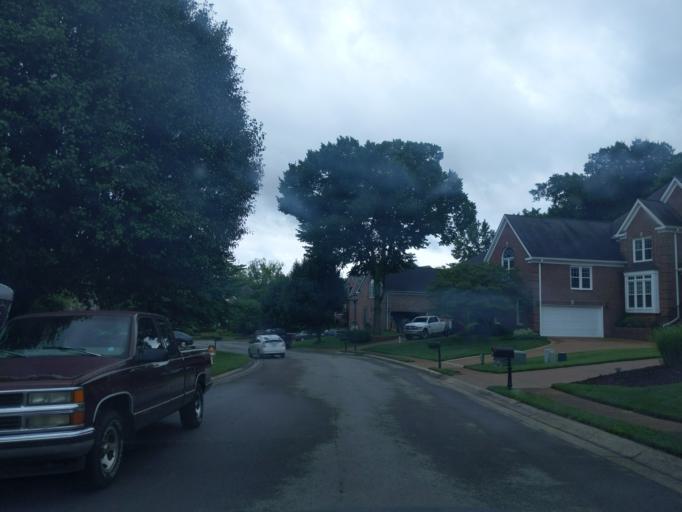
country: US
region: Tennessee
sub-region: Williamson County
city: Brentwood
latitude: 36.0422
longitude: -86.7543
